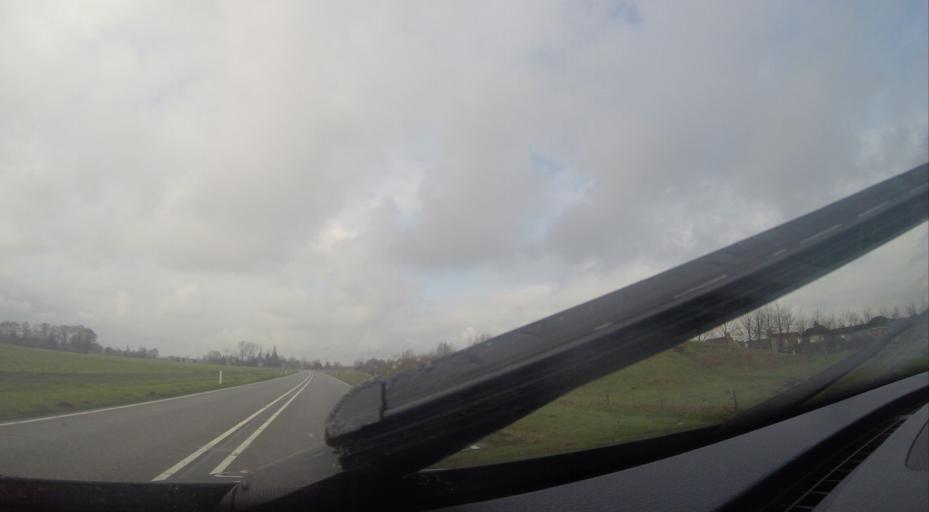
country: NL
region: Gelderland
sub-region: Gemeente Bronckhorst
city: Zelhem
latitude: 52.0014
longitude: 6.3396
